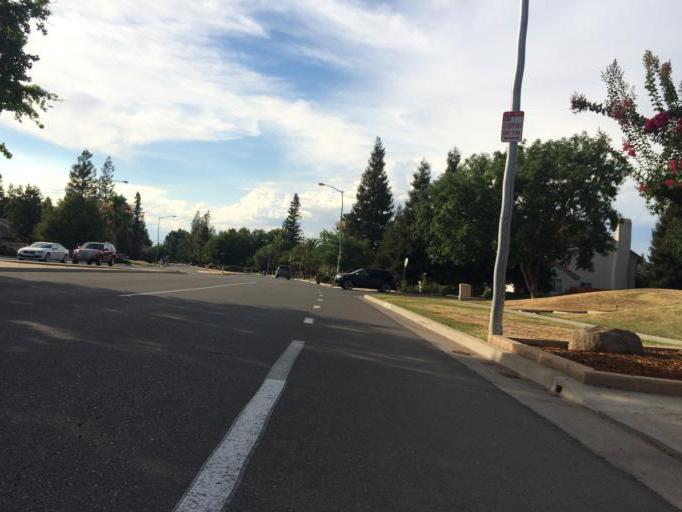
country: US
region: California
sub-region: Fresno County
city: Clovis
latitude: 36.8559
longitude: -119.7751
